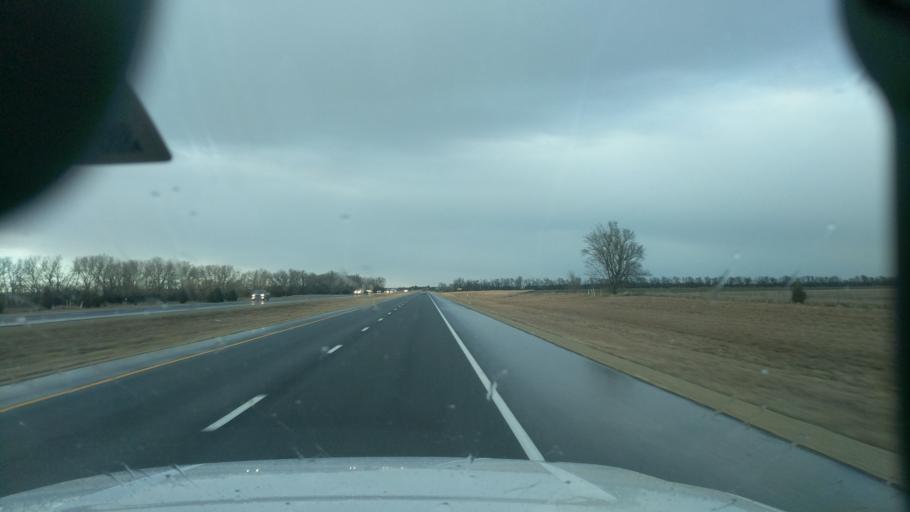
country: US
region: Kansas
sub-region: Harvey County
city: Newton
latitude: 37.9712
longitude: -97.3270
